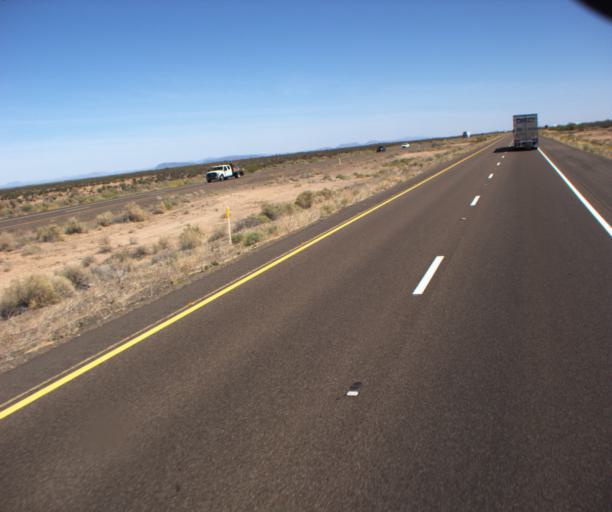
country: US
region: Arizona
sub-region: Yuma County
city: Wellton
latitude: 32.8146
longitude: -113.5036
